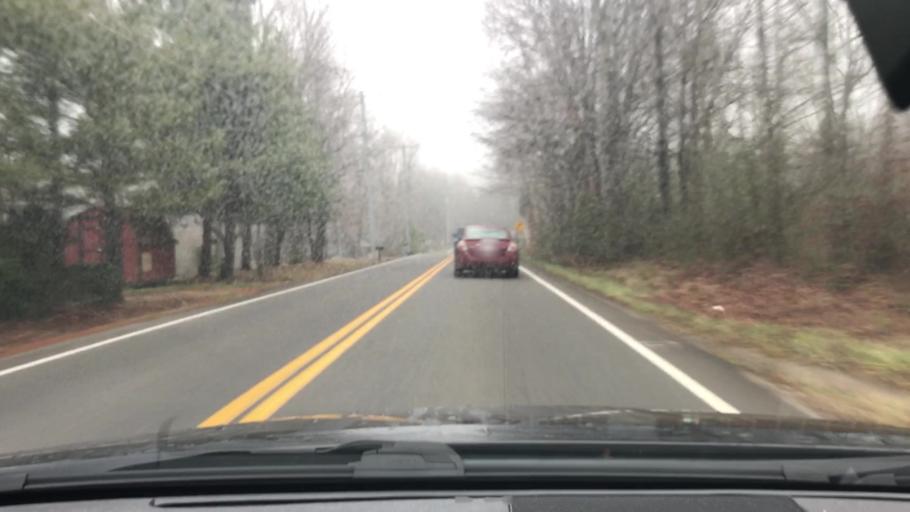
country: US
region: Tennessee
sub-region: Cheatham County
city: Ashland City
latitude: 36.2816
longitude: -87.1822
